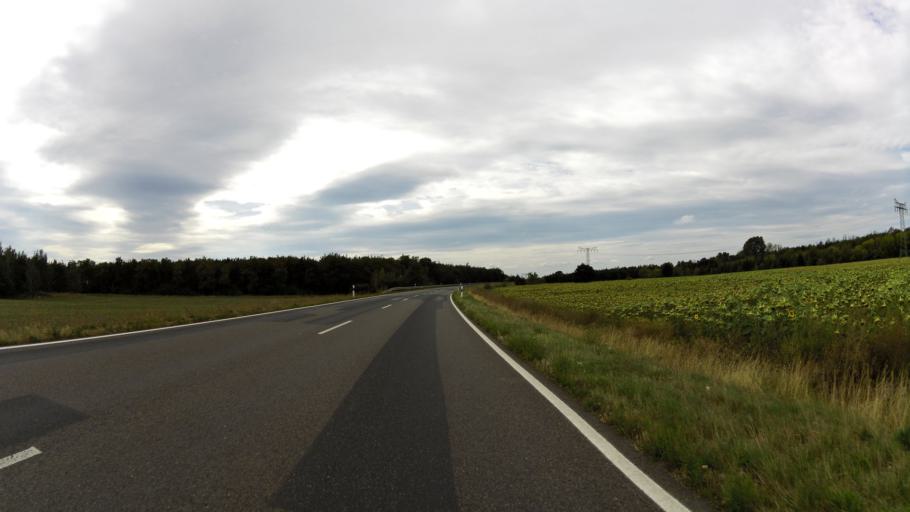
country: DE
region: Brandenburg
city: Heinersbruck
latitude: 51.8169
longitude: 14.5197
